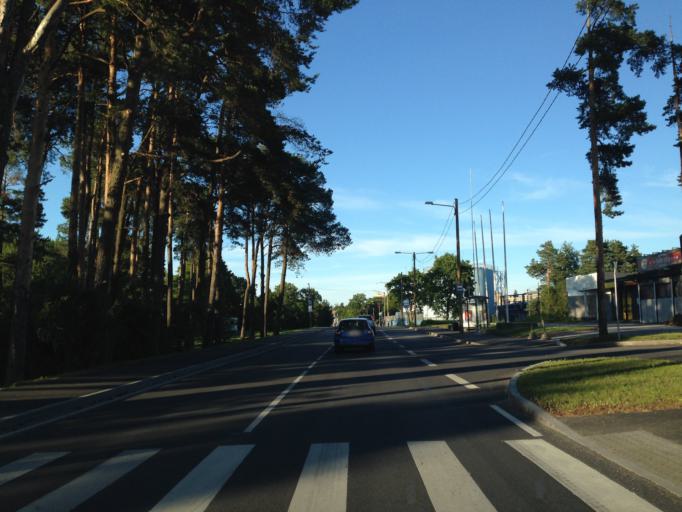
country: EE
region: Harju
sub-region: Saue vald
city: Laagri
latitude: 59.4008
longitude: 24.6475
